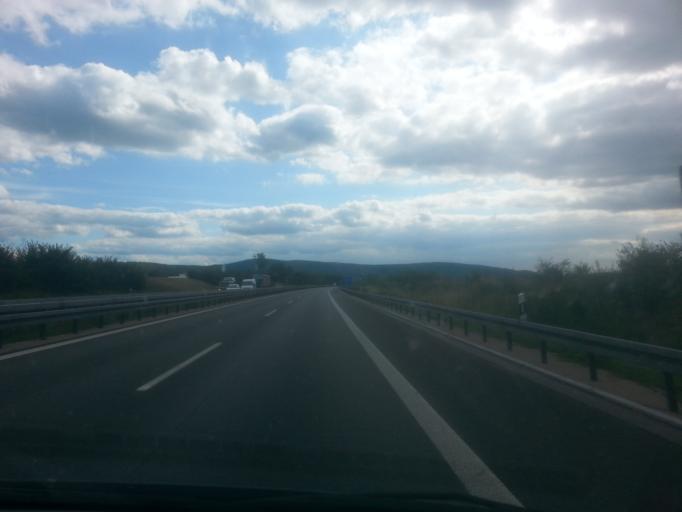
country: DE
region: Bavaria
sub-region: Upper Palatinate
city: Nabburg
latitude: 49.4639
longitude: 12.1949
